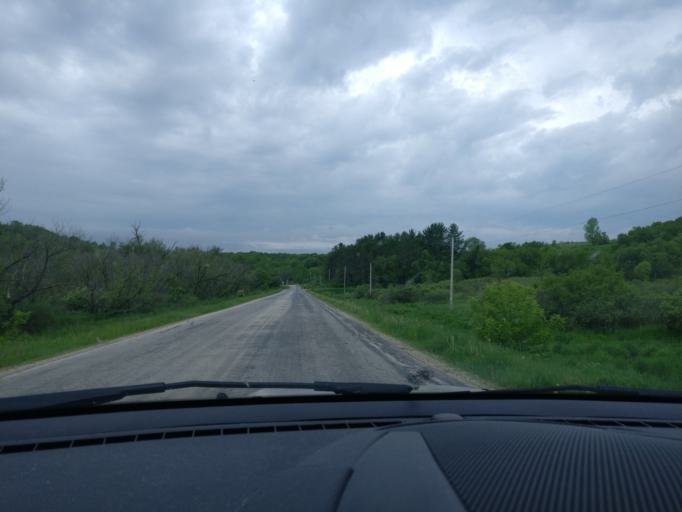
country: US
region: Wisconsin
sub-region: Lafayette County
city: Darlington
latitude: 42.7764
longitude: -89.9958
